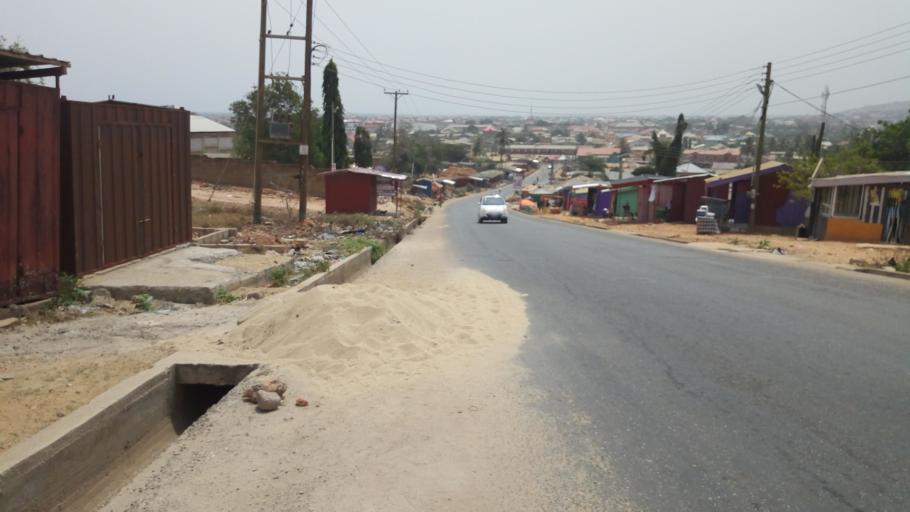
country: GH
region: Greater Accra
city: Gbawe
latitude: 5.5613
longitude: -0.3098
